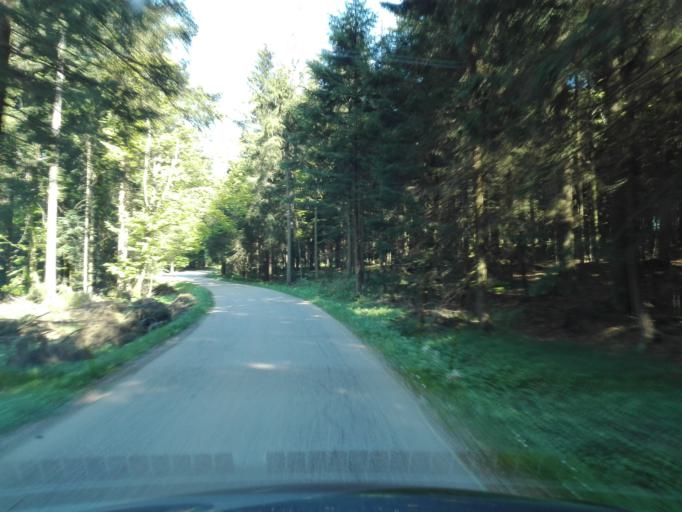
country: DE
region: Bavaria
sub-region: Lower Bavaria
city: Obernzell
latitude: 48.4391
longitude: 13.6916
